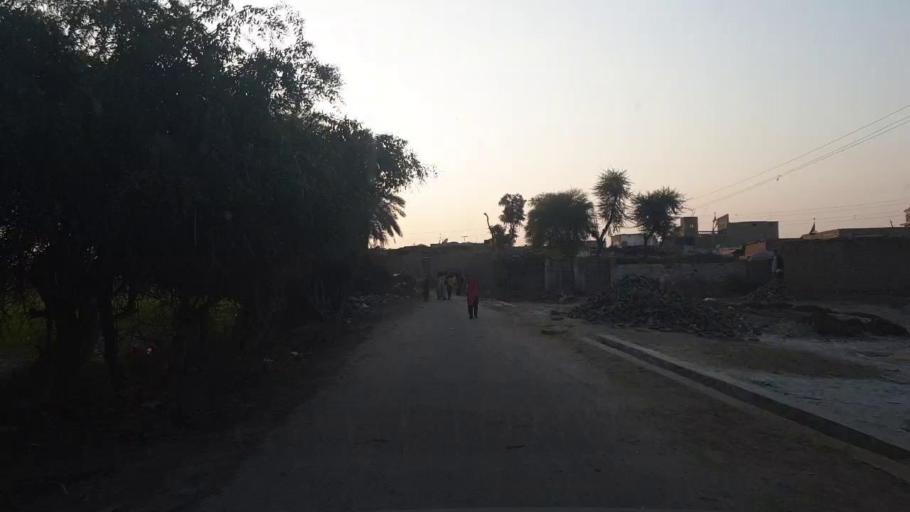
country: PK
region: Sindh
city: Bhit Shah
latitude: 25.8758
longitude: 68.5442
